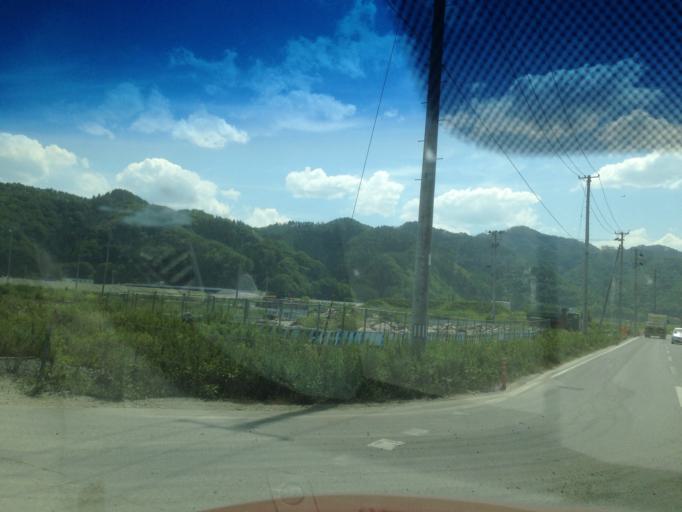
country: JP
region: Iwate
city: Otsuchi
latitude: 39.3579
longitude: 141.9074
